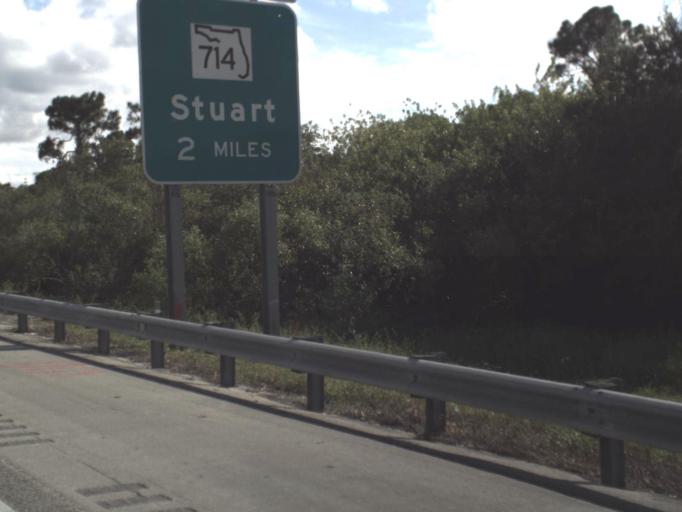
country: US
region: Florida
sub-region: Martin County
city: Palm City
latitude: 27.1847
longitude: -80.3205
